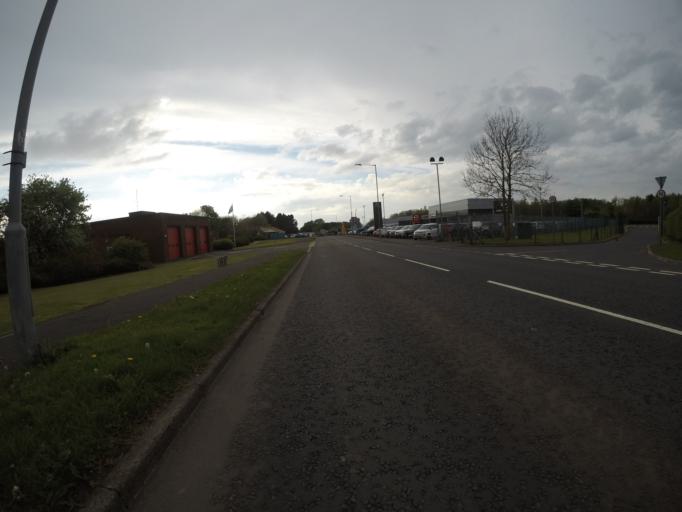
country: GB
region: Scotland
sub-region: North Ayrshire
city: Dreghorn
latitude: 55.6076
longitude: -4.6342
